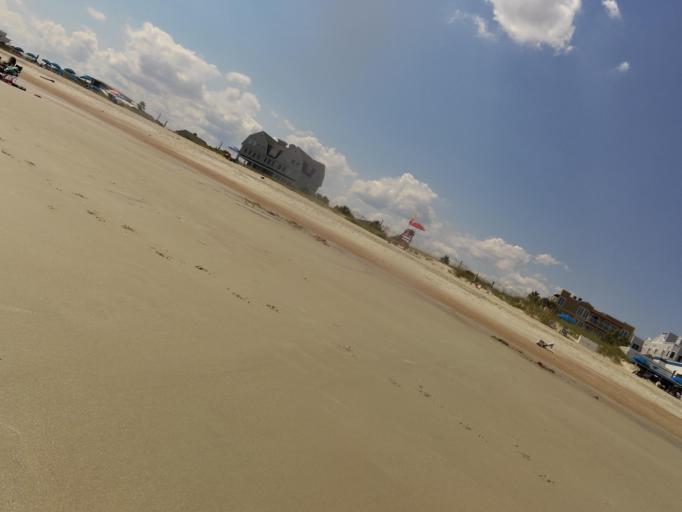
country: US
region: Florida
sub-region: Nassau County
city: Fernandina Beach
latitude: 30.6668
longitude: -81.4299
